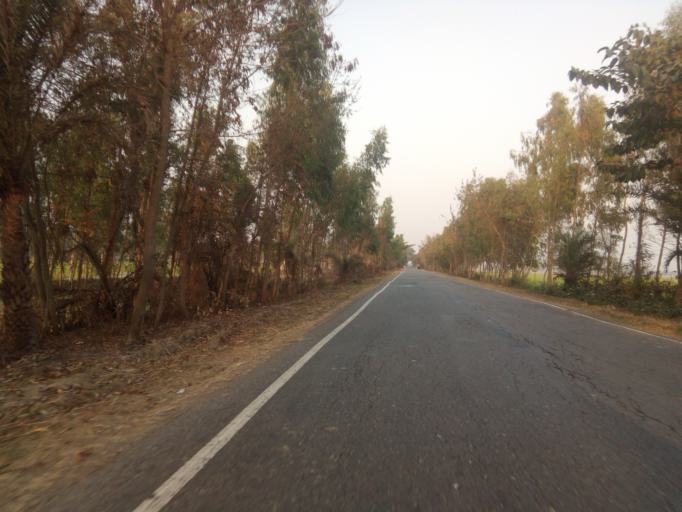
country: BD
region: Rajshahi
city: Bogra
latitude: 24.5753
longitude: 89.2193
